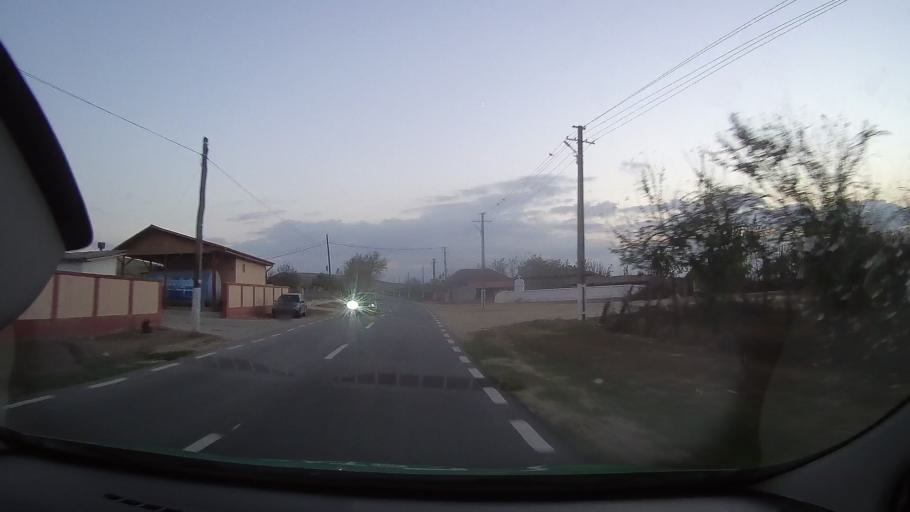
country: RO
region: Constanta
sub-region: Comuna Oltina
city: Oltina
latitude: 44.1579
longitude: 27.6674
